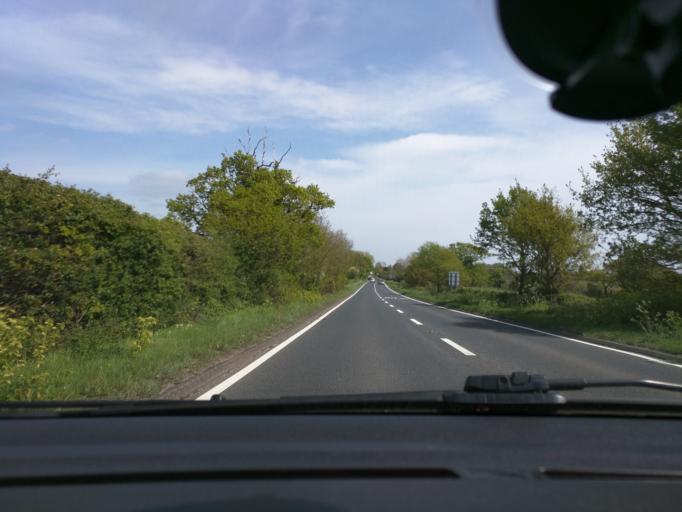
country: GB
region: England
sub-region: Suffolk
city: Halesworth
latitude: 52.2792
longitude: 1.5318
